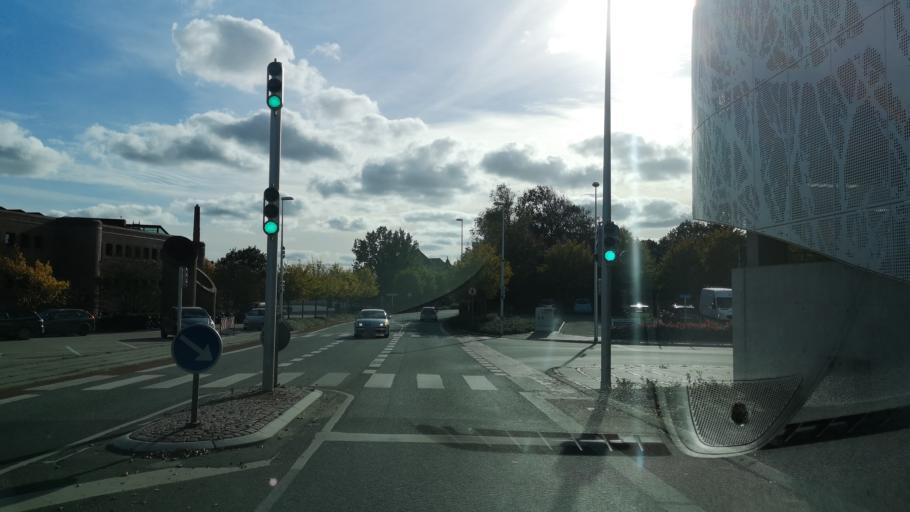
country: DK
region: Central Jutland
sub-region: Holstebro Kommune
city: Holstebro
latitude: 56.3607
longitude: 8.6150
